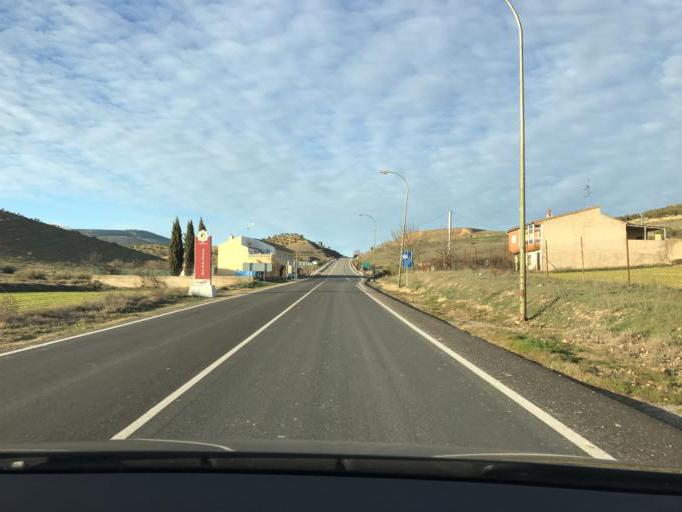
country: ES
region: Andalusia
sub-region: Provincia de Jaen
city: Guadahortuna
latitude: 37.5630
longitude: -3.4007
